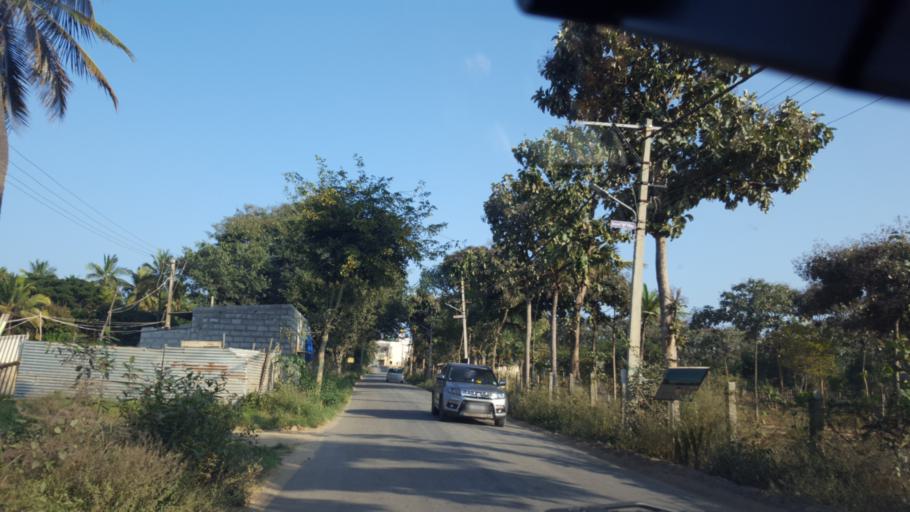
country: IN
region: Karnataka
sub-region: Bangalore Rural
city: Hoskote
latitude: 12.9168
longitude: 77.7634
